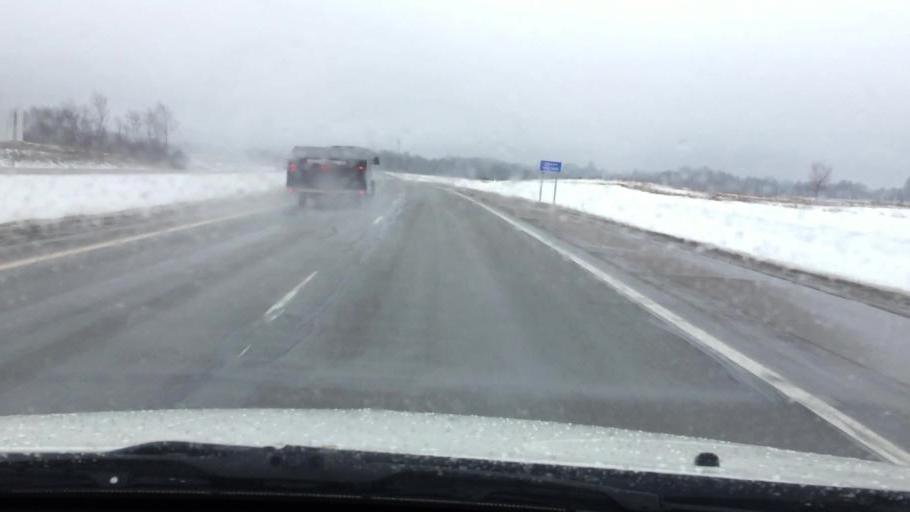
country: US
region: Michigan
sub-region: Wexford County
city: Cadillac
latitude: 44.2609
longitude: -85.3841
